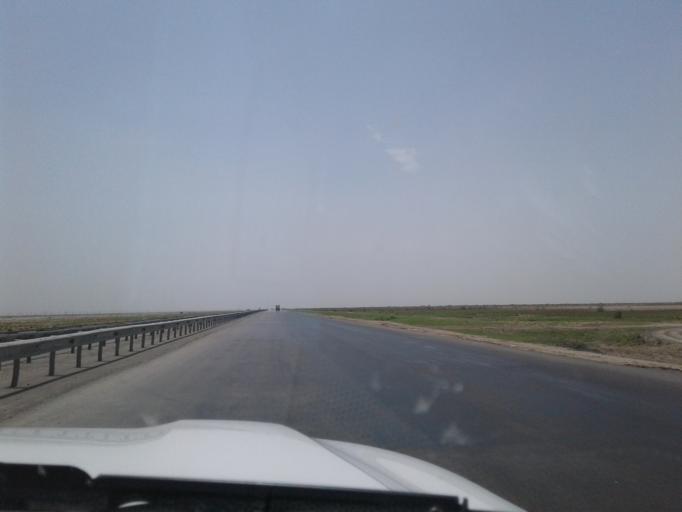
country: TM
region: Ahal
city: Tejen
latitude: 37.3418
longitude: 60.3925
